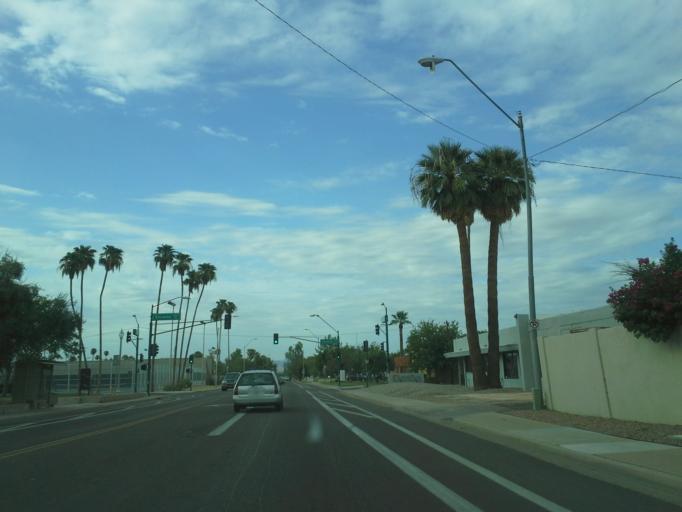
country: US
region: Arizona
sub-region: Maricopa County
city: Phoenix
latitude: 33.4739
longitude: -112.0914
